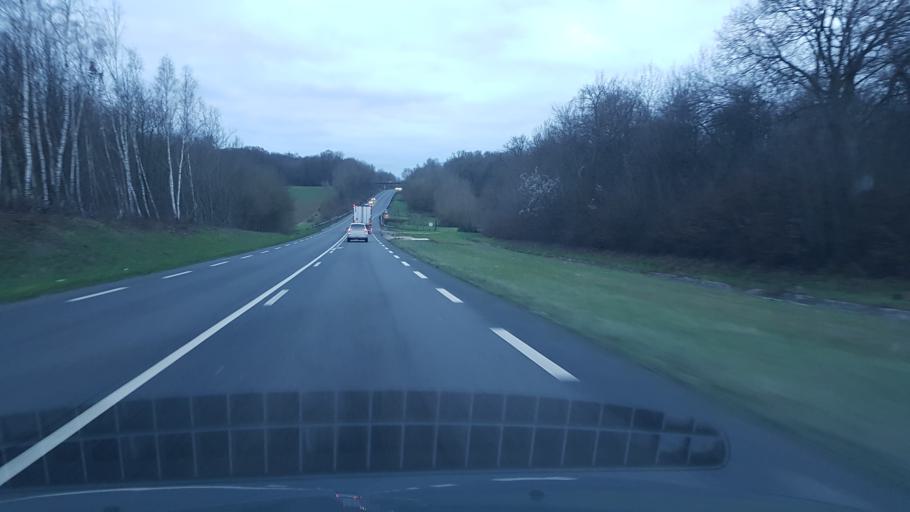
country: FR
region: Ile-de-France
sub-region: Departement de Seine-et-Marne
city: Guignes
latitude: 48.6593
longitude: 2.8079
